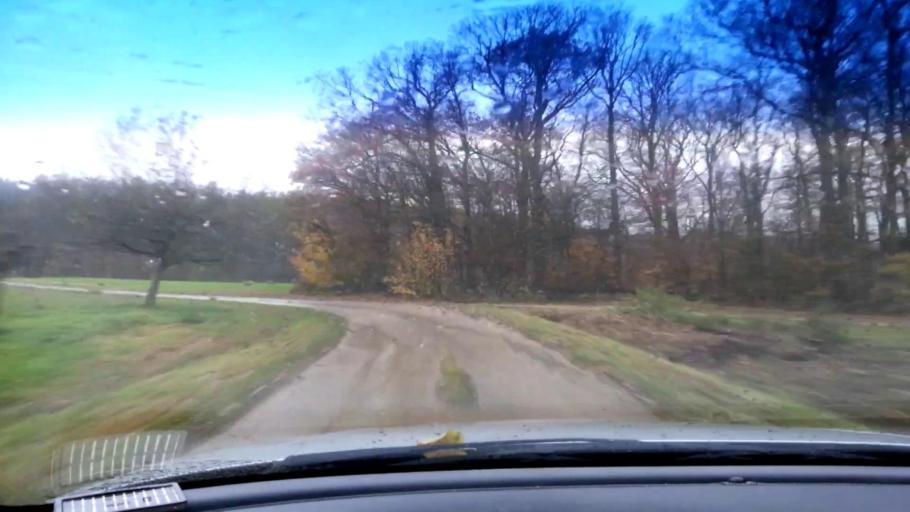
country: DE
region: Bavaria
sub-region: Upper Franconia
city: Schesslitz
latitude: 49.9465
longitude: 11.0288
